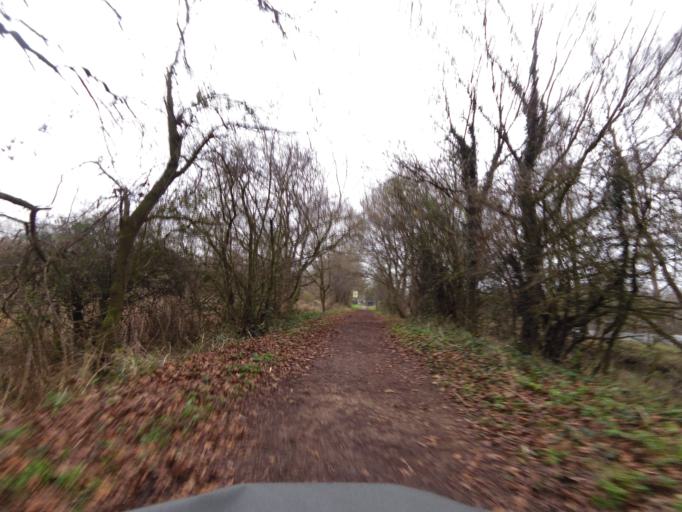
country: GB
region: England
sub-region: Norfolk
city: Mattishall
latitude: 52.7244
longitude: 1.1123
